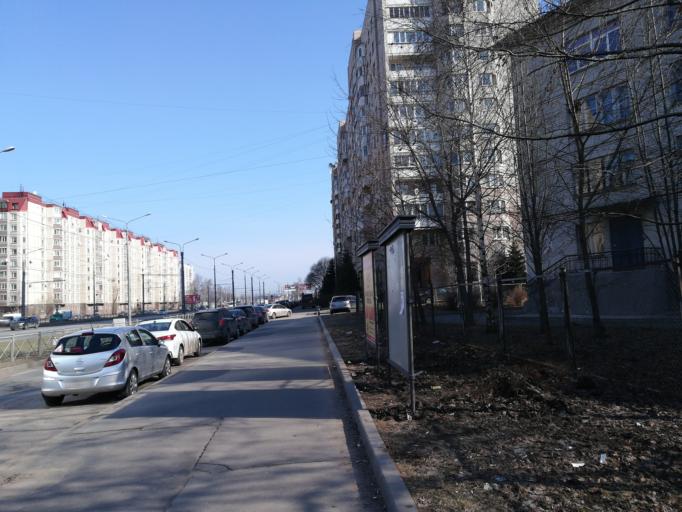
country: RU
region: St.-Petersburg
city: Vasyl'evsky Ostrov
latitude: 59.9520
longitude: 30.2347
